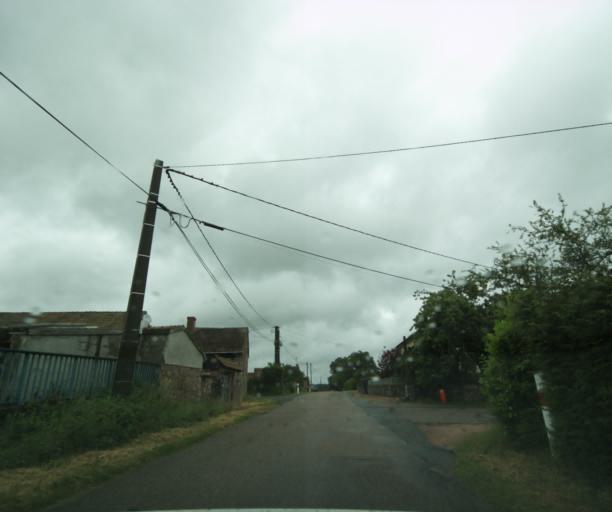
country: FR
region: Bourgogne
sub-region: Departement de Saone-et-Loire
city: Charolles
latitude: 46.4599
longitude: 4.4350
